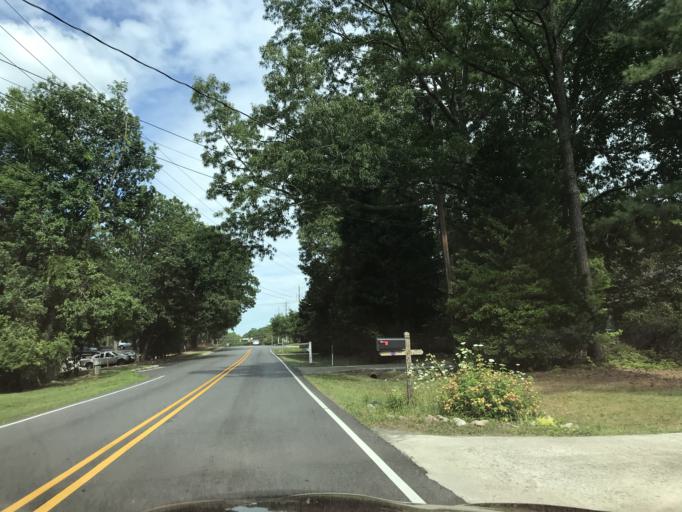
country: US
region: North Carolina
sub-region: Wake County
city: West Raleigh
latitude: 35.8895
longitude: -78.6826
